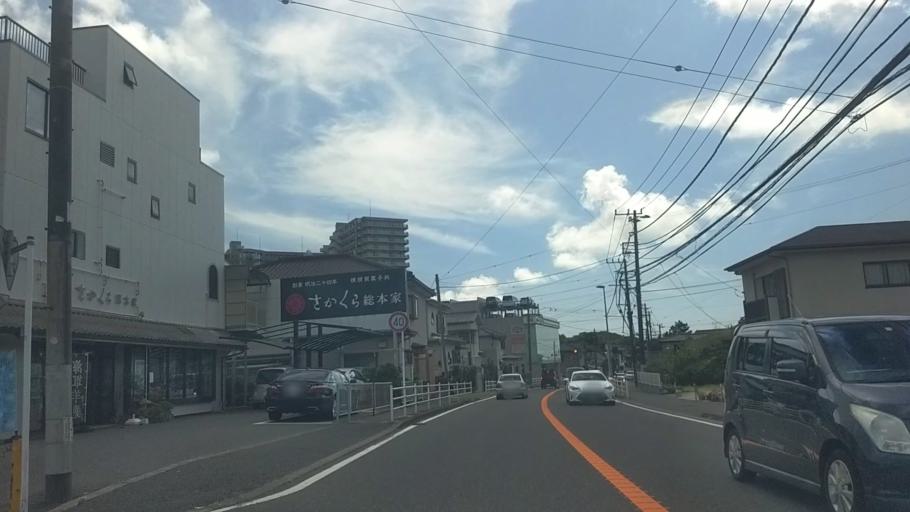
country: JP
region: Kanagawa
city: Yokosuka
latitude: 35.2241
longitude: 139.6446
